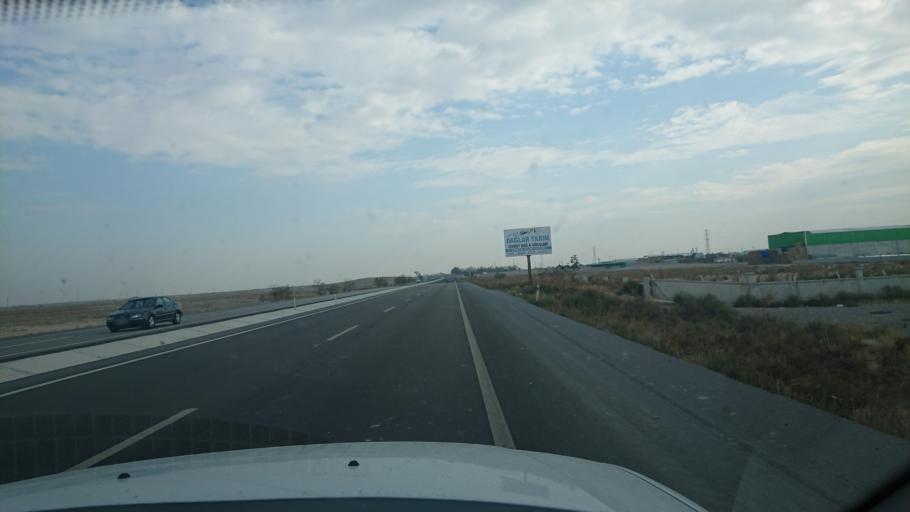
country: TR
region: Aksaray
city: Yesilova
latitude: 38.2935
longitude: 33.7706
